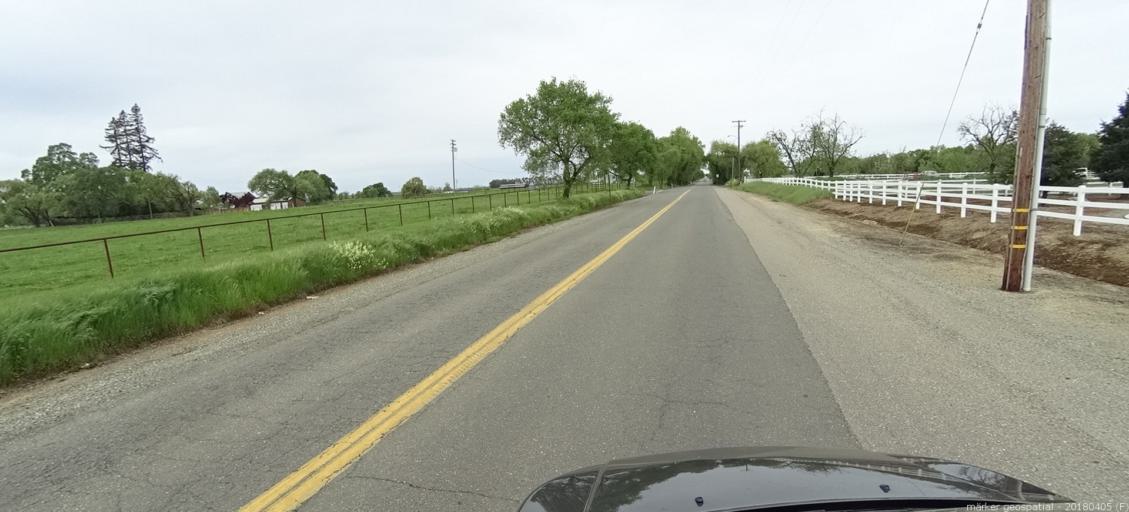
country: US
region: California
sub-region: Sacramento County
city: Galt
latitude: 38.2756
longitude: -121.3372
